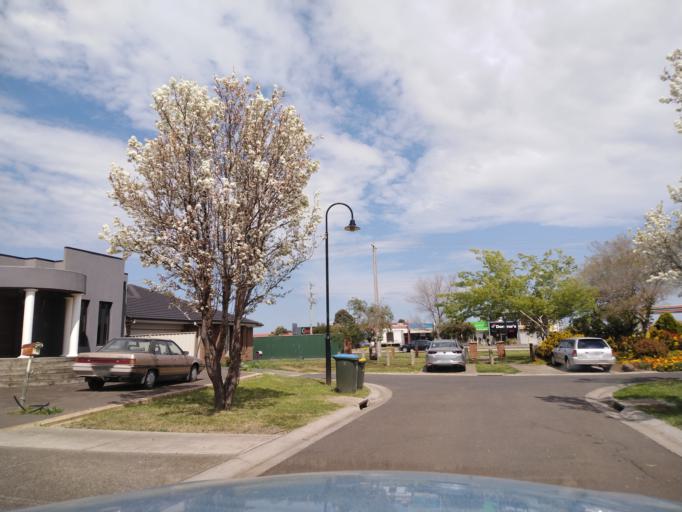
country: AU
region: Victoria
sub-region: Wyndham
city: Hoppers Crossing
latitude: -37.8500
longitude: 144.7076
